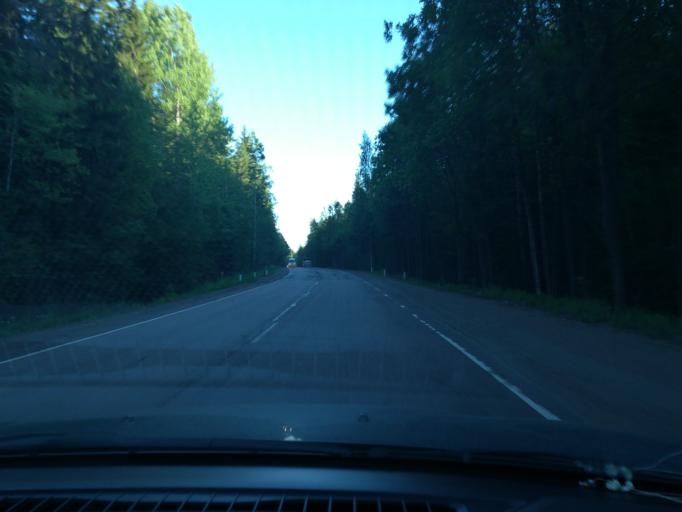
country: RU
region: Leningrad
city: Lesogorskiy
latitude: 60.9858
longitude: 28.9083
